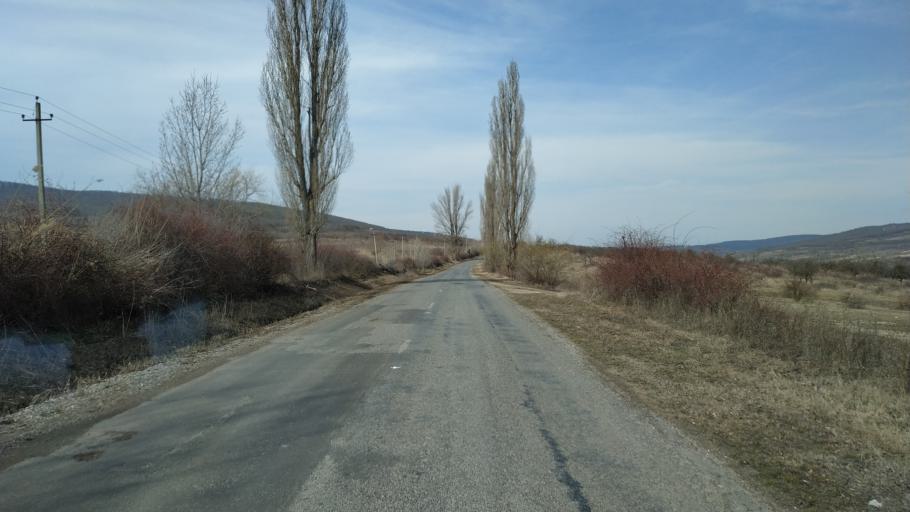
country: MD
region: Nisporeni
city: Nisporeni
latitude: 47.1709
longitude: 28.0919
